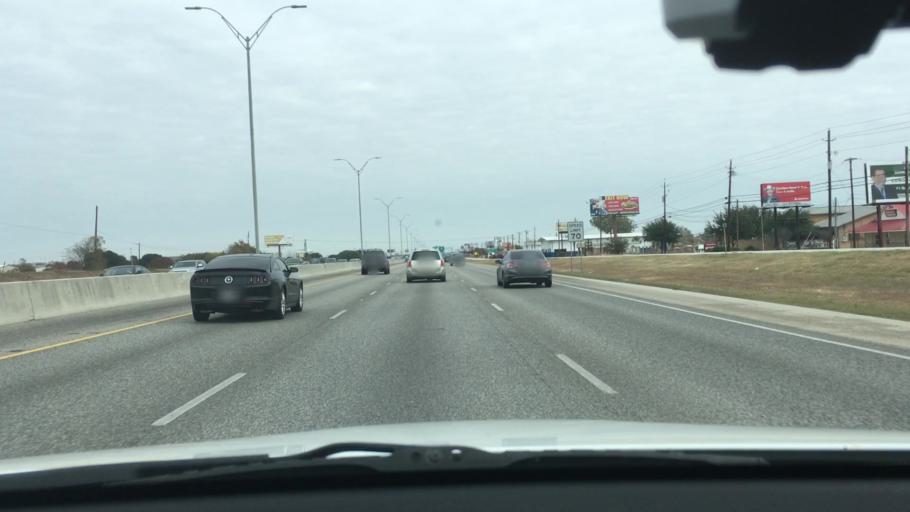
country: US
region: Texas
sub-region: Hays County
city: San Marcos
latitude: 29.8484
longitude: -97.9624
